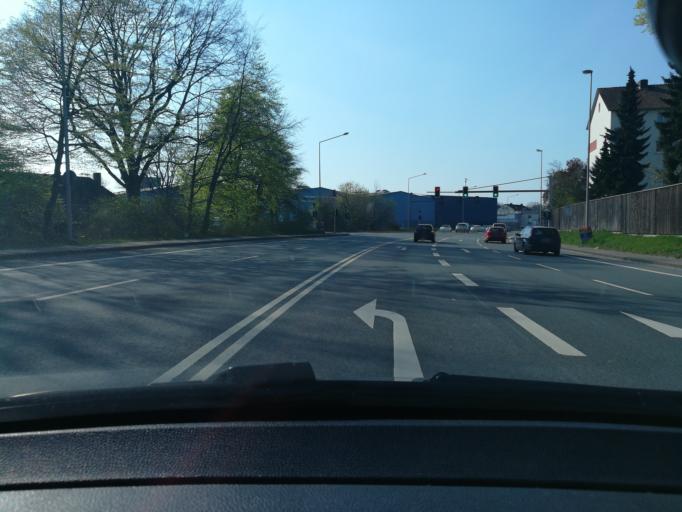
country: DE
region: North Rhine-Westphalia
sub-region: Regierungsbezirk Detmold
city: Bielefeld
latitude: 51.9760
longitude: 8.5104
